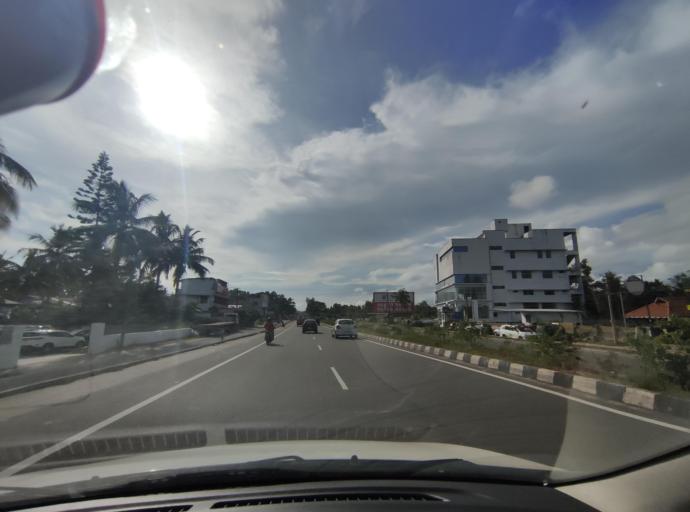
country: IN
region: Kerala
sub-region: Thiruvananthapuram
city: Thiruvananthapuram
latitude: 8.4990
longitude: 76.9158
